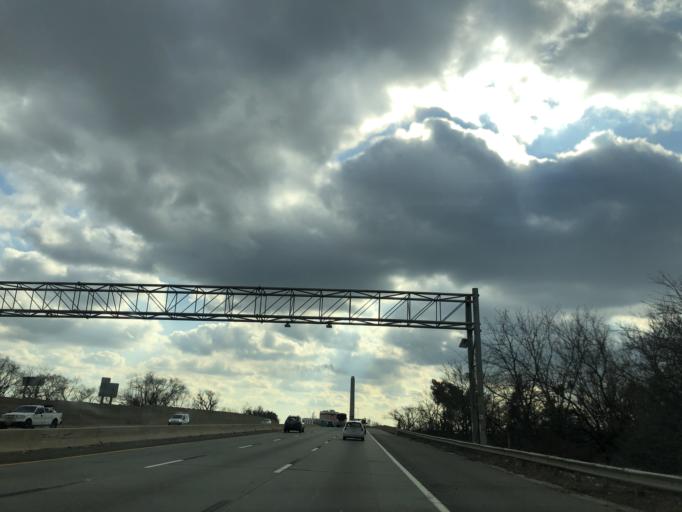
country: US
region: New Jersey
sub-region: Camden County
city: Camden
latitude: 39.9194
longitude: -75.1165
